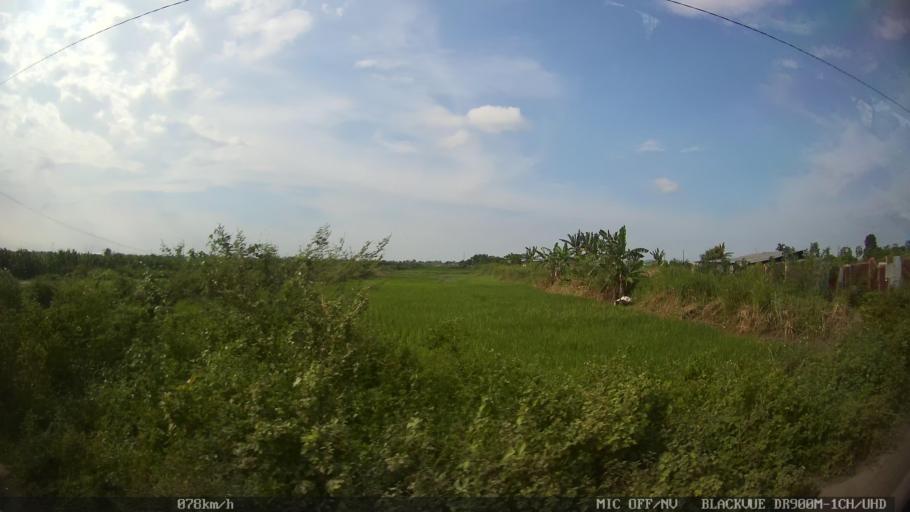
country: ID
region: North Sumatra
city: Medan
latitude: 3.5730
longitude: 98.7706
